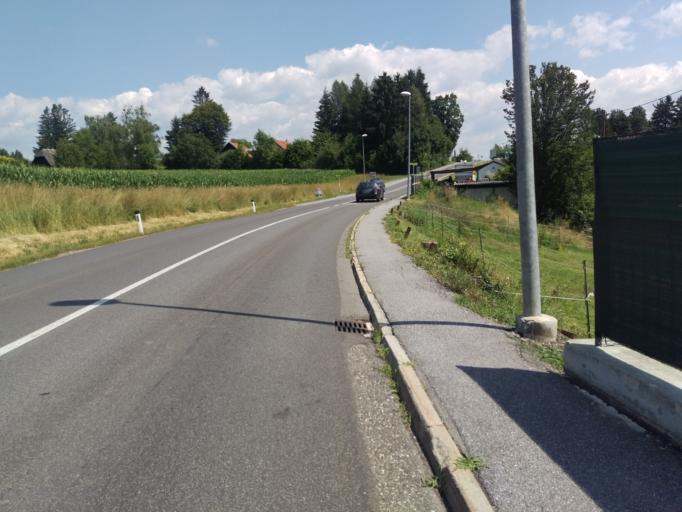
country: AT
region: Styria
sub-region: Politischer Bezirk Graz-Umgebung
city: Kumberg
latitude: 47.1479
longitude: 15.5160
